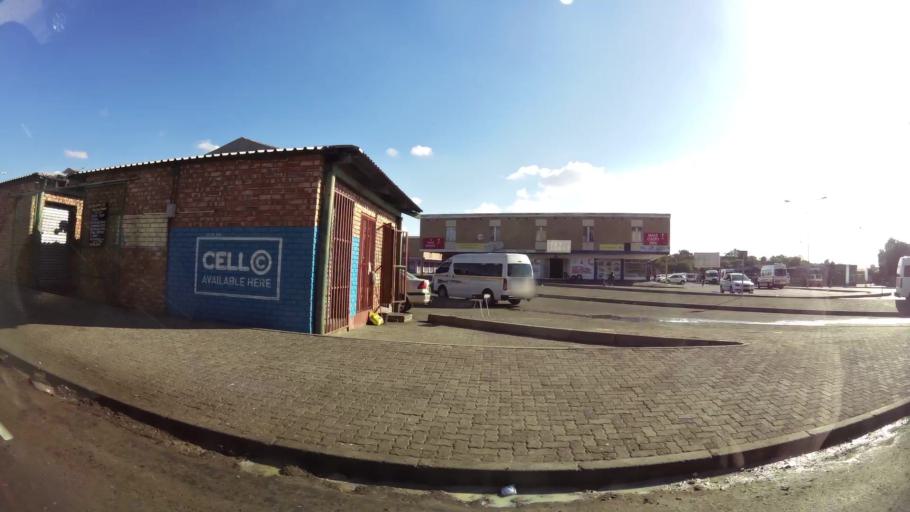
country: ZA
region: Northern Cape
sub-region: Frances Baard District Municipality
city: Kimberley
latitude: -28.7342
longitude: 24.7618
